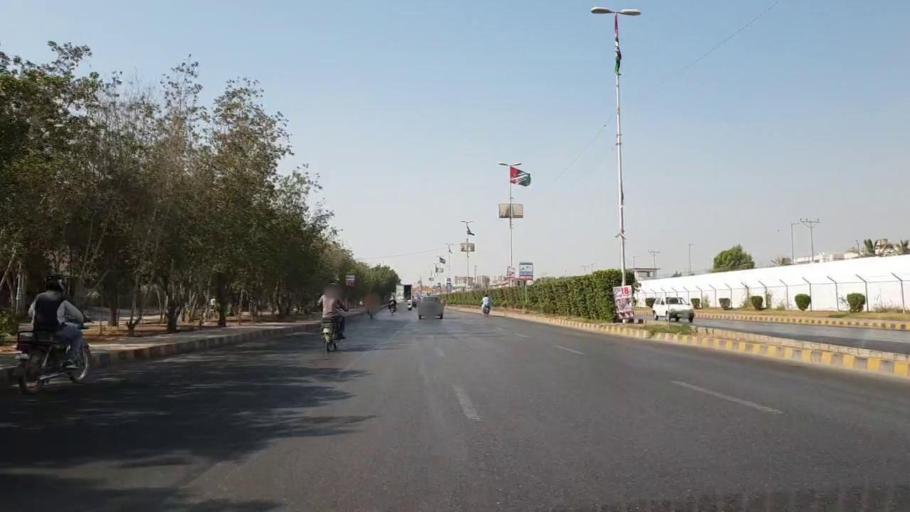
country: PK
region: Sindh
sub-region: Karachi District
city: Karachi
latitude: 24.8773
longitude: 67.0947
